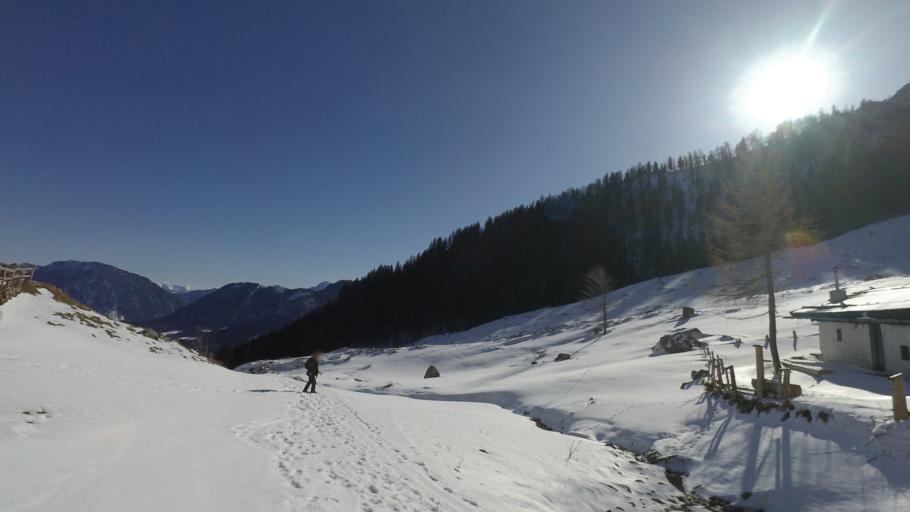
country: DE
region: Bavaria
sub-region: Upper Bavaria
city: Bergen
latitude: 47.7571
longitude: 12.5827
